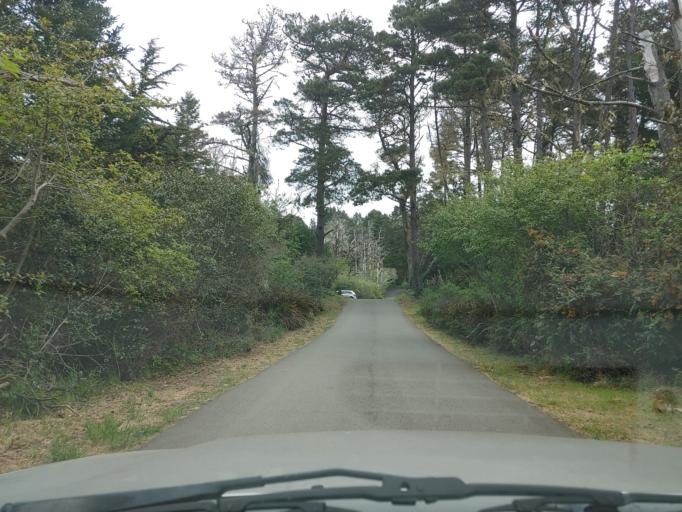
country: US
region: California
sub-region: Mendocino County
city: Fort Bragg
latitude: 39.3297
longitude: -123.8087
